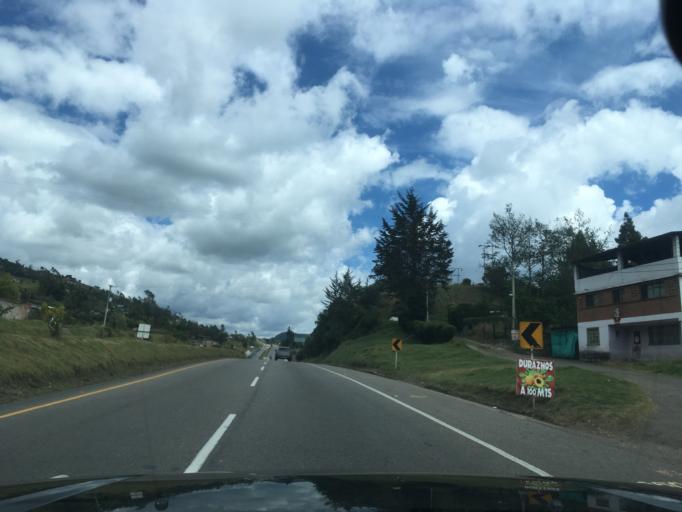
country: CO
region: Boyaca
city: Ventaquemada
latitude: 5.3739
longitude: -73.5156
